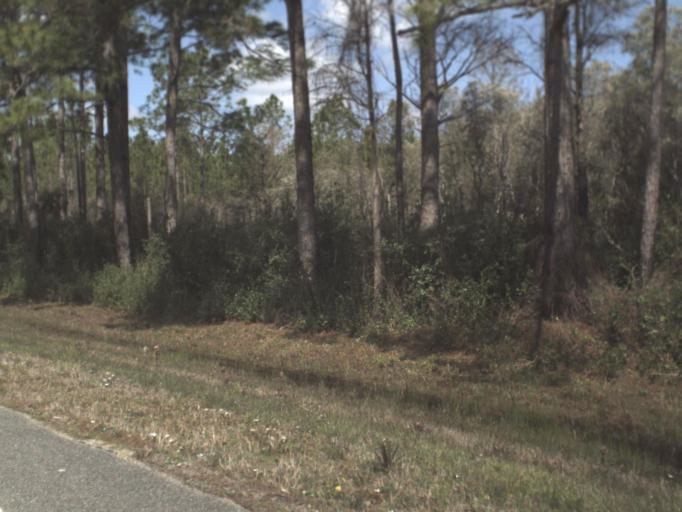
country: US
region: Florida
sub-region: Franklin County
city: Apalachicola
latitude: 29.7325
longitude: -85.1457
